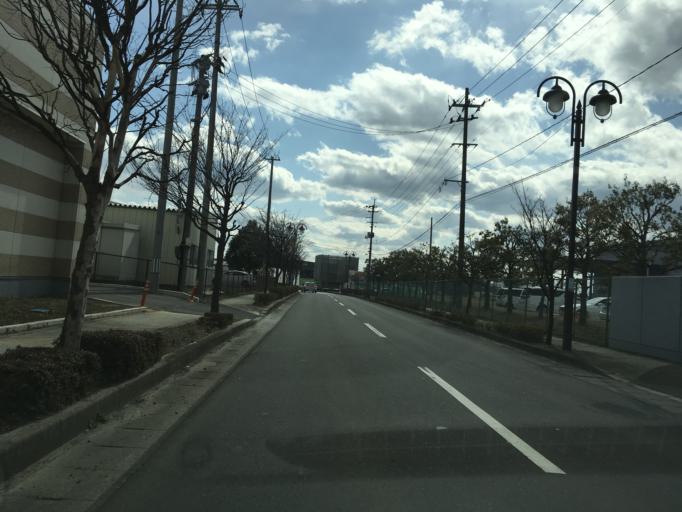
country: JP
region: Miyagi
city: Wakuya
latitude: 38.6979
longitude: 141.2092
